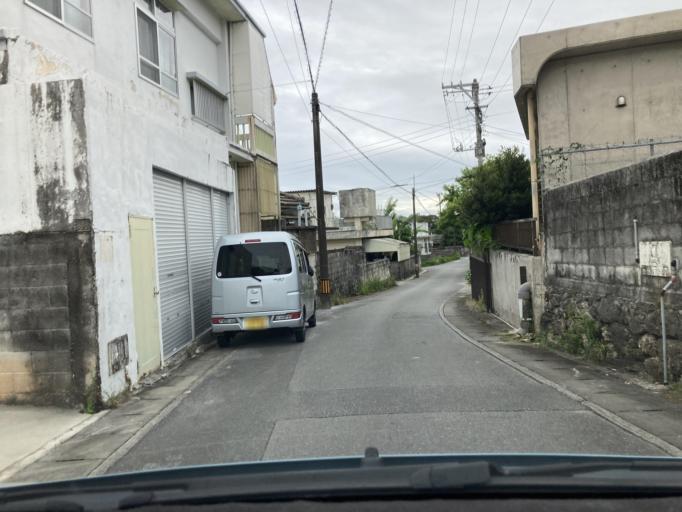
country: JP
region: Okinawa
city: Tomigusuku
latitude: 26.1747
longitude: 127.7141
